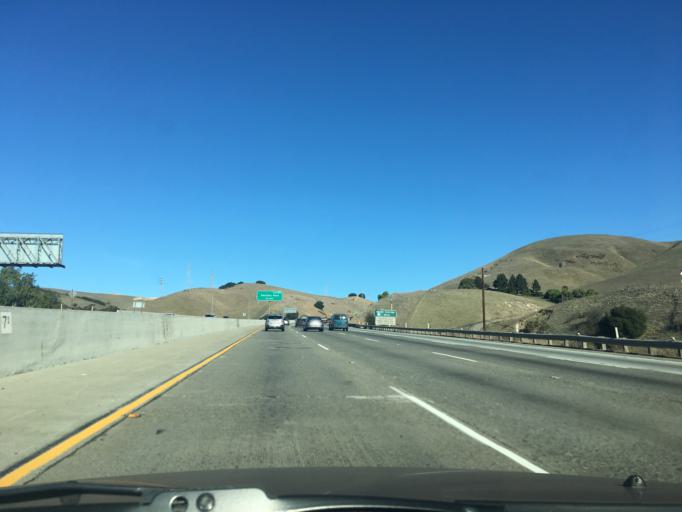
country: US
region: California
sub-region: Alameda County
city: Fremont
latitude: 37.5531
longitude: -121.9173
